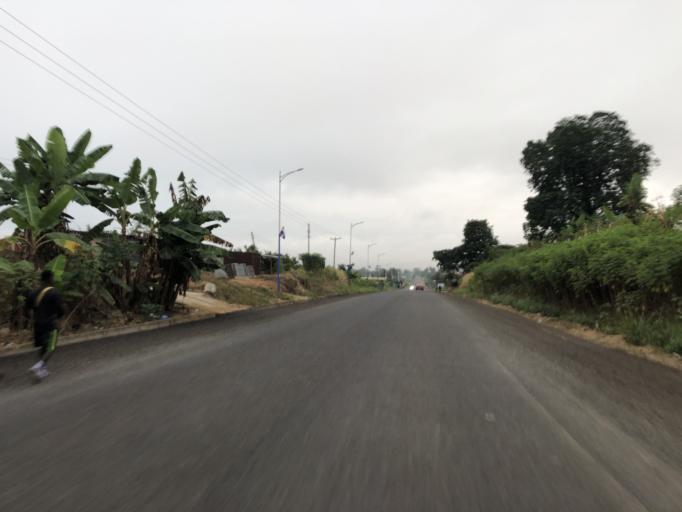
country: GH
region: Eastern
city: Koforidua
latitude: 6.1957
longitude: -0.3615
